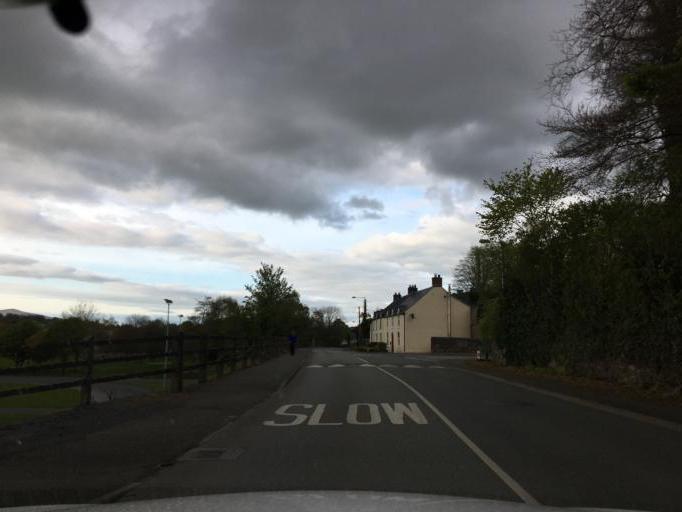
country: IE
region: Leinster
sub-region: Loch Garman
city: New Ross
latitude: 52.3887
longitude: -6.9494
